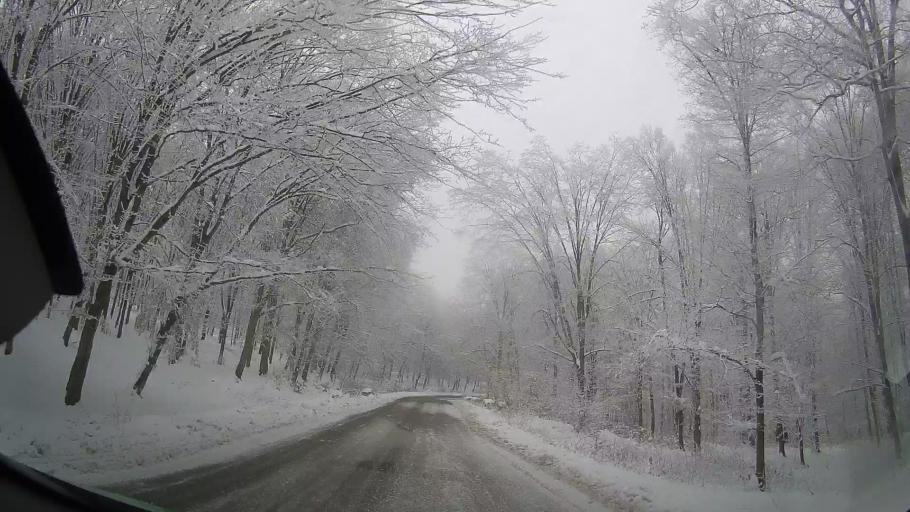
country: RO
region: Neamt
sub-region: Comuna Valea Ursului
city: Valea Ursului
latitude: 46.8385
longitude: 27.0692
